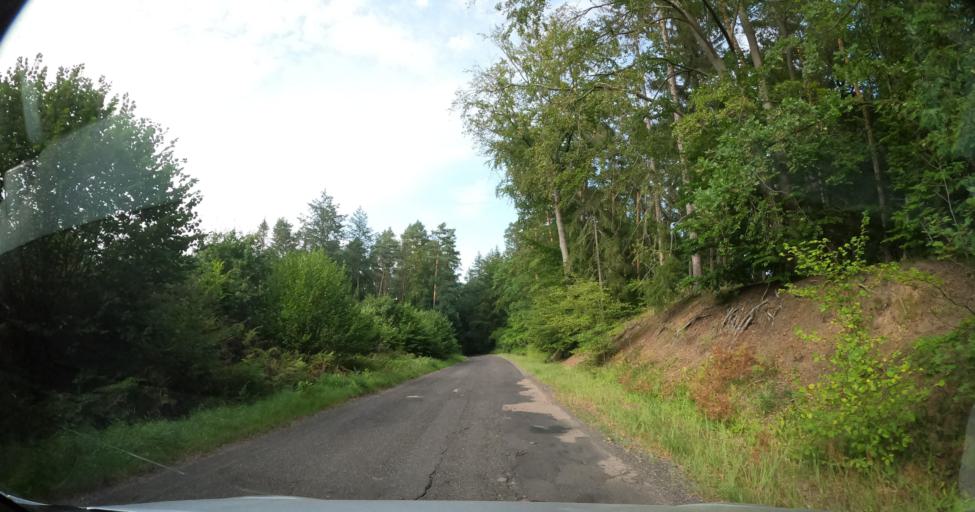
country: PL
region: West Pomeranian Voivodeship
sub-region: Powiat goleniowski
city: Goleniow
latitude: 53.5381
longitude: 14.8466
